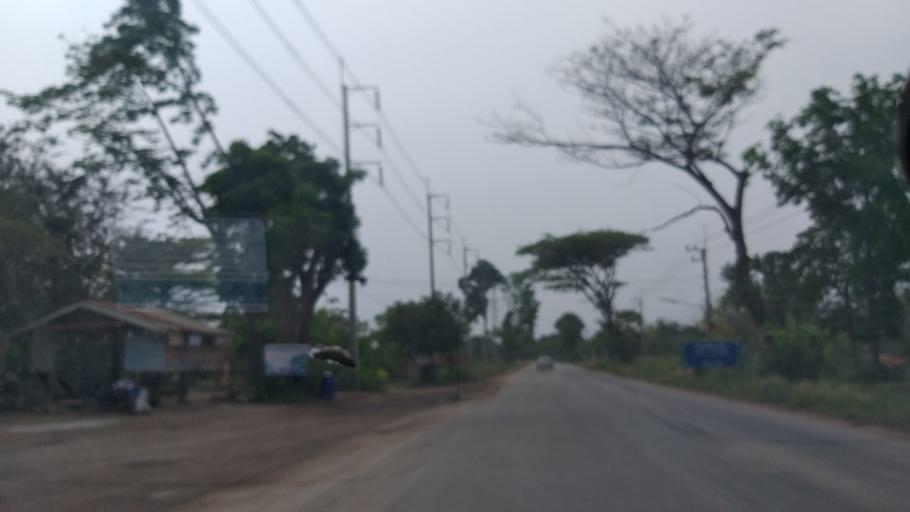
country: TH
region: Chachoengsao
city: Plaeng Yao
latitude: 13.5738
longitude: 101.2582
